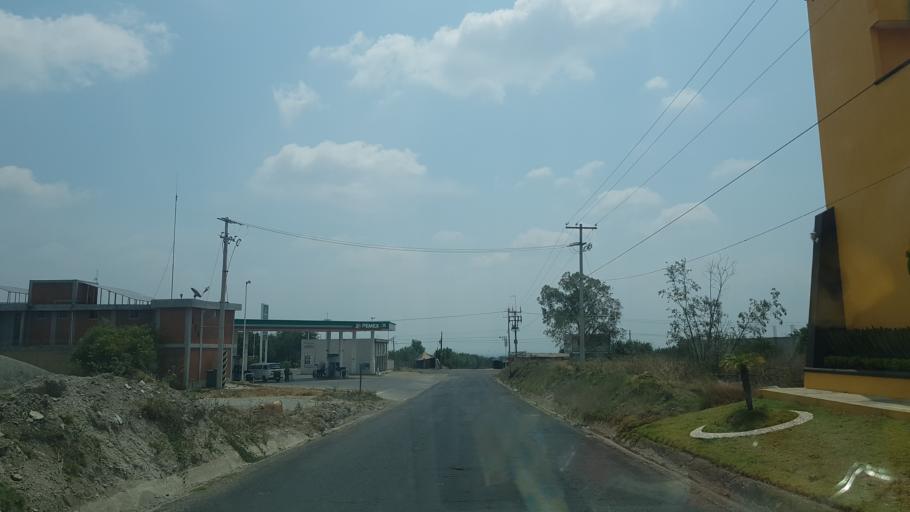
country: MX
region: Puebla
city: Huejotzingo
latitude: 19.1363
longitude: -98.4156
